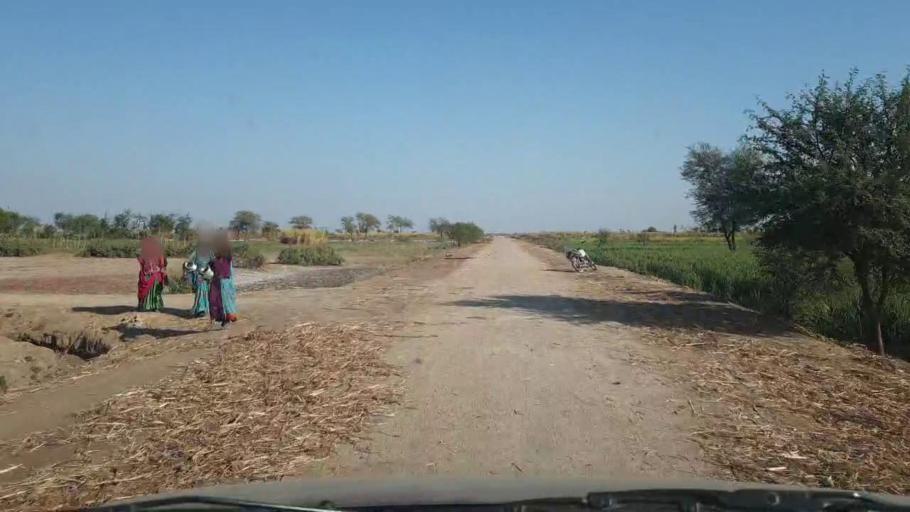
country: PK
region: Sindh
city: Samaro
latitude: 25.3488
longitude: 69.3193
